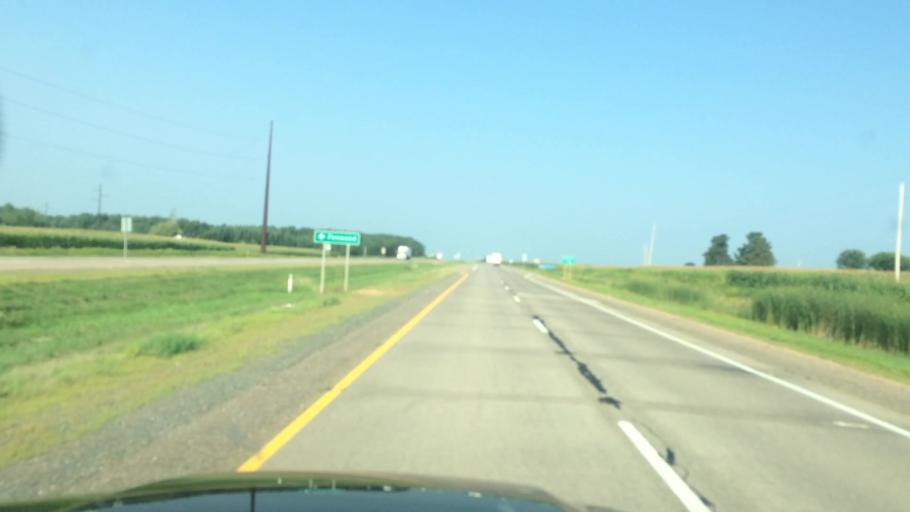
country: US
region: Wisconsin
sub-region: Marathon County
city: Edgar
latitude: 44.9444
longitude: -90.0212
